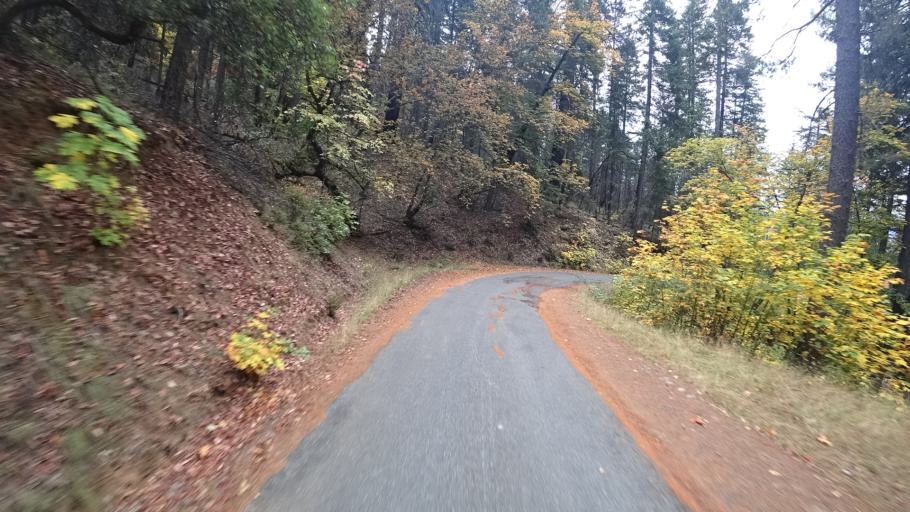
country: US
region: California
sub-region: Siskiyou County
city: Happy Camp
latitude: 41.8154
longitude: -123.3324
